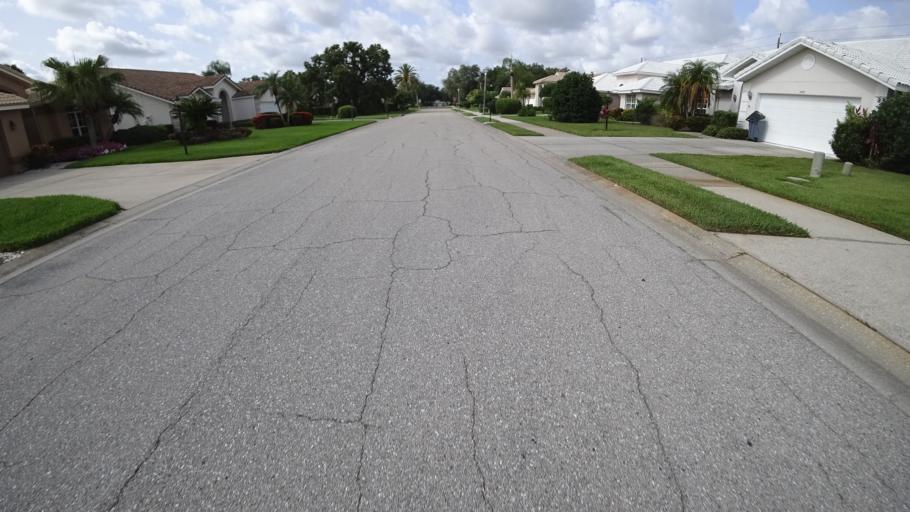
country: US
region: Florida
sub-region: Manatee County
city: Samoset
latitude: 27.4399
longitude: -82.4804
